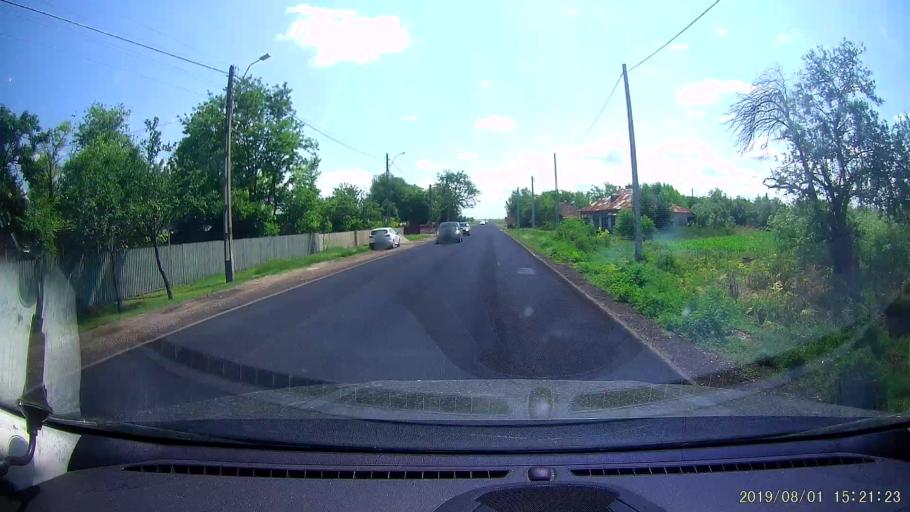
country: RO
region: Braila
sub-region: Comuna Tufesti
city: Tufesti
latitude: 45.0704
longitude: 27.7966
